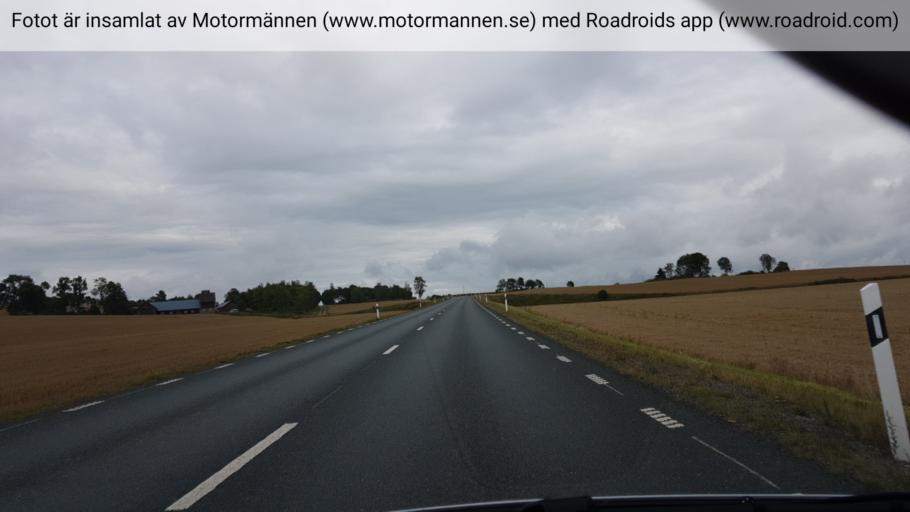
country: SE
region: Vaestra Goetaland
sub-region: Falkopings Kommun
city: Akarp
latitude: 58.1230
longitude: 13.7514
